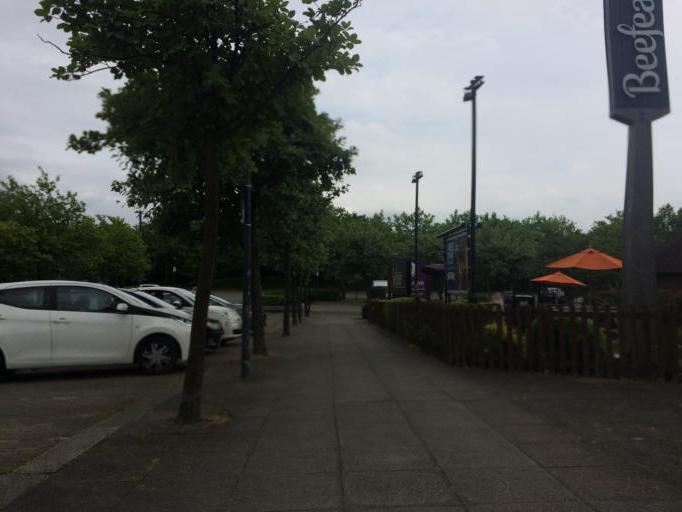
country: GB
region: England
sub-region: Milton Keynes
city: Milton Keynes
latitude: 52.0401
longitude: -0.7517
